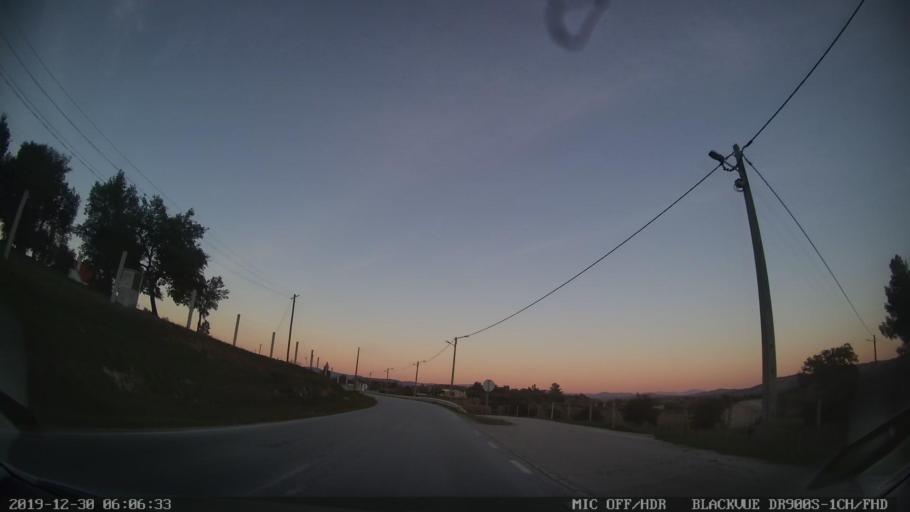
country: PT
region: Castelo Branco
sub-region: Penamacor
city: Penamacor
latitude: 40.0996
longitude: -7.2302
